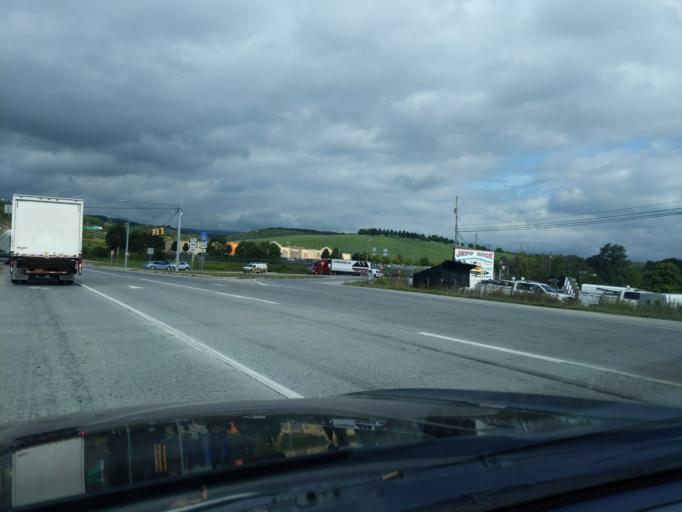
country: US
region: Pennsylvania
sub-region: Blair County
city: Roaring Spring
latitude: 40.3680
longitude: -78.4288
